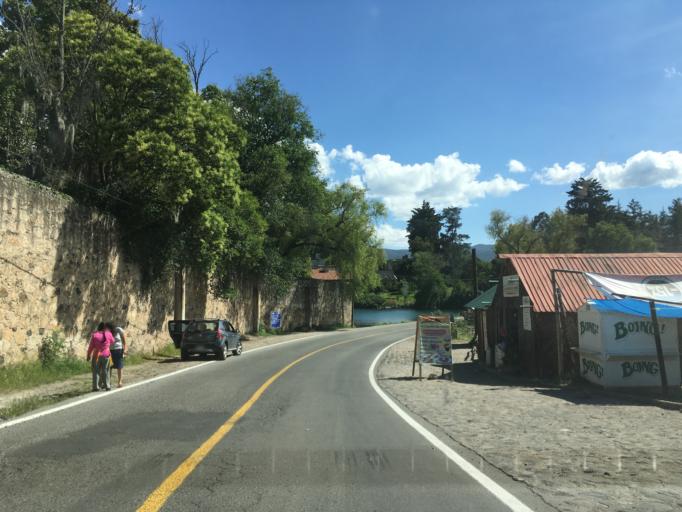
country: MX
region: Hidalgo
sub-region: Omitlan de Juarez
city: San Antonio el Paso
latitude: 20.2224
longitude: -98.5595
